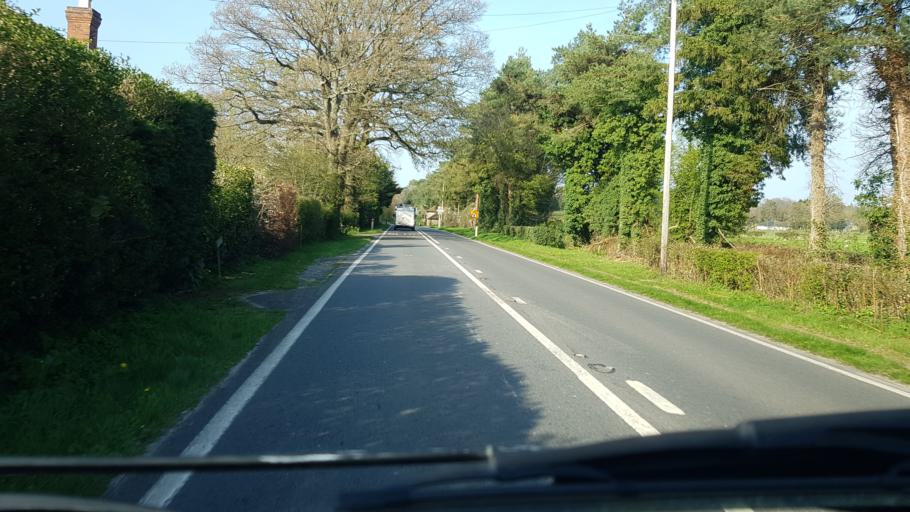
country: GB
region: England
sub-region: West Sussex
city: Petworth
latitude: 50.9557
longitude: -0.6282
